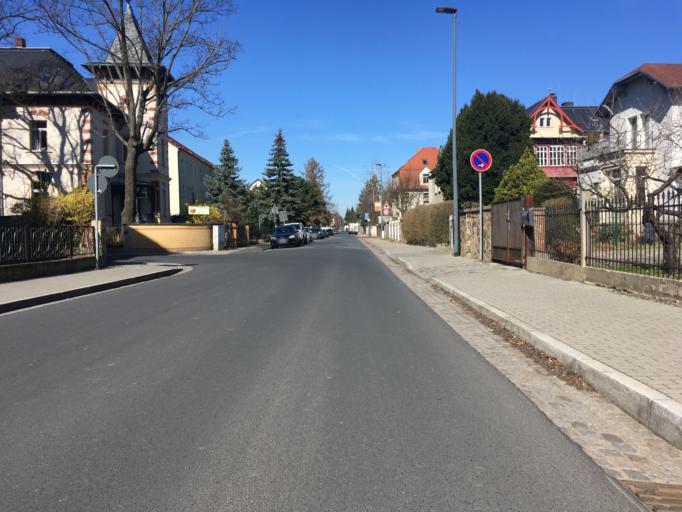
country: DE
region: Saxony
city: Radebeul
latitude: 51.1072
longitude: 13.6255
